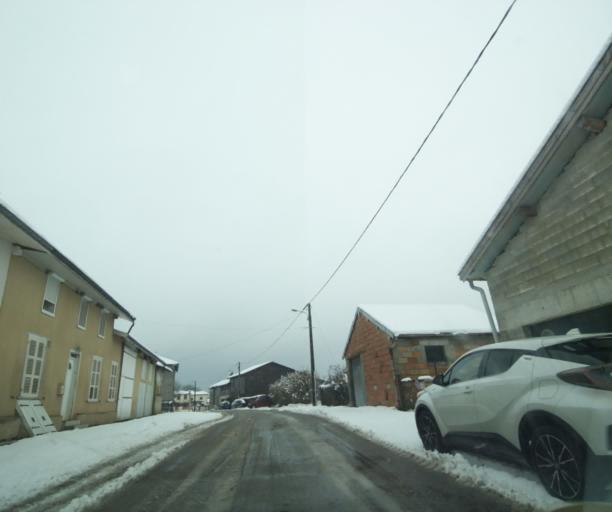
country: FR
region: Champagne-Ardenne
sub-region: Departement de la Haute-Marne
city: Montier-en-Der
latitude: 48.5067
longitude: 4.7843
